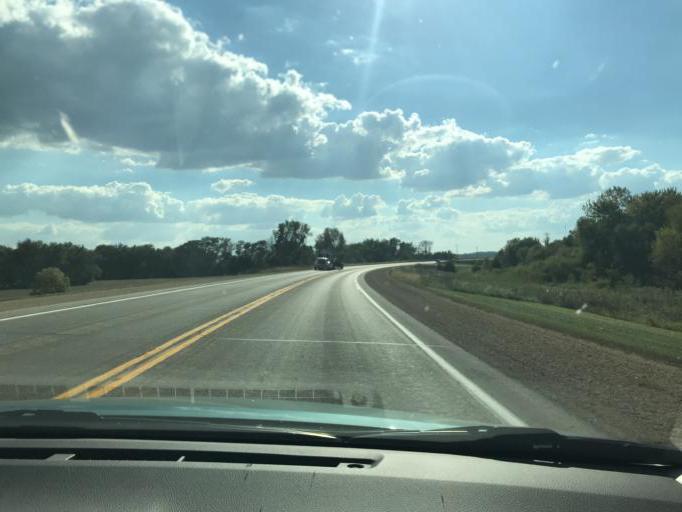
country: US
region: Wisconsin
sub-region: Green County
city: Brodhead
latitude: 42.5885
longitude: -89.4015
